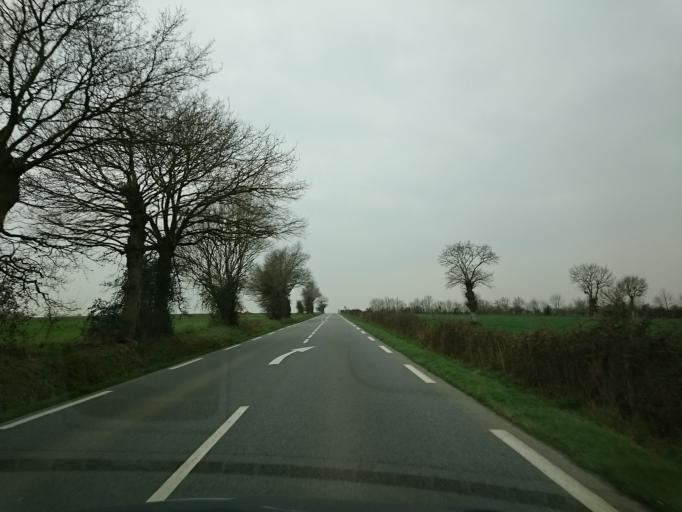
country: FR
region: Brittany
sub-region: Departement d'Ille-et-Vilaine
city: Pance
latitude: 47.8698
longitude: -1.6554
